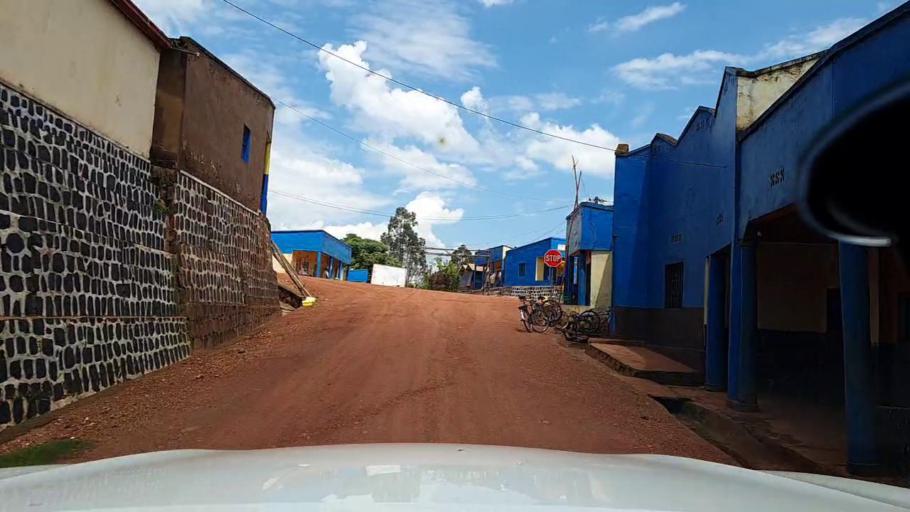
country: RW
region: Northern Province
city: Byumba
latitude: -1.7357
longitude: 29.8571
